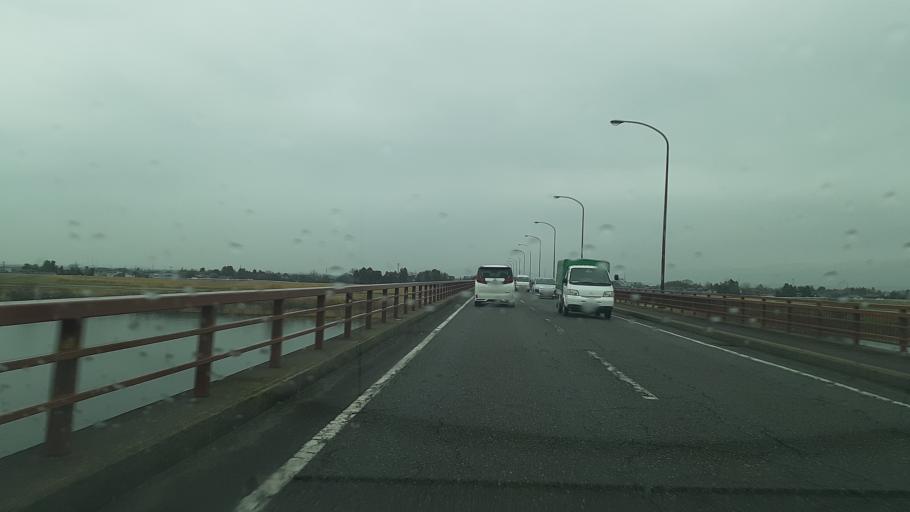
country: JP
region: Niigata
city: Kameda-honcho
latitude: 37.8791
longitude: 139.1647
